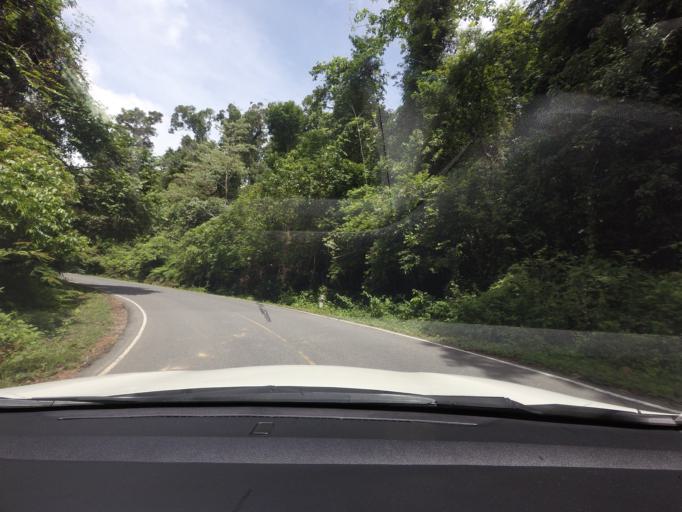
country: TH
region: Nakhon Nayok
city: Nakhon Nayok
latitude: 14.3423
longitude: 101.3487
